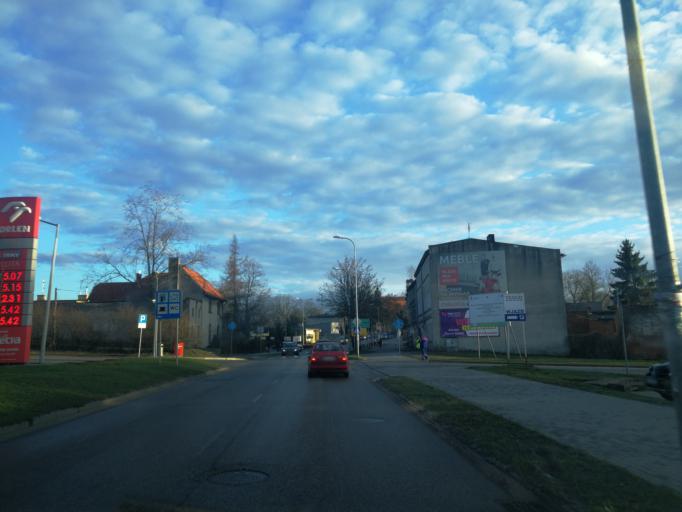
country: PL
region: Kujawsko-Pomorskie
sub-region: Powiat torunski
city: Chelmza
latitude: 53.1908
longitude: 18.6138
